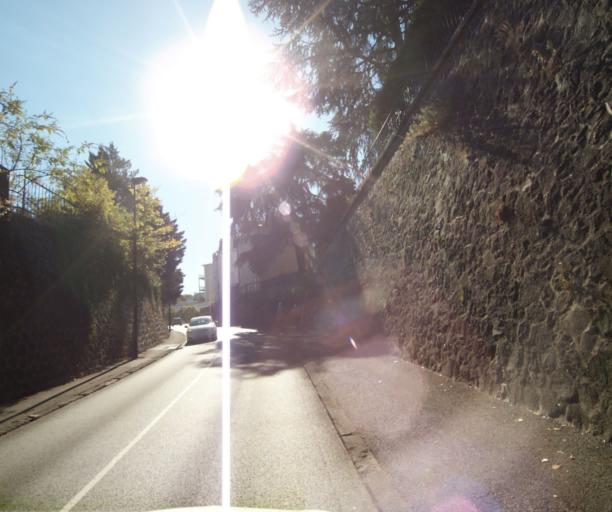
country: FR
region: Auvergne
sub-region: Departement du Puy-de-Dome
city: Chamalieres
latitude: 45.7685
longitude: 3.0603
